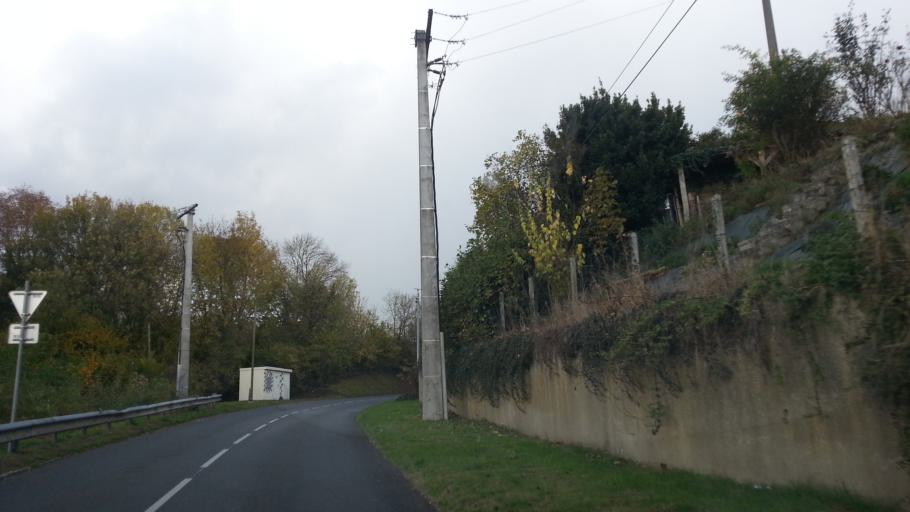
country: FR
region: Picardie
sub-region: Departement de l'Oise
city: Thiverny
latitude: 49.2514
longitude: 2.4045
